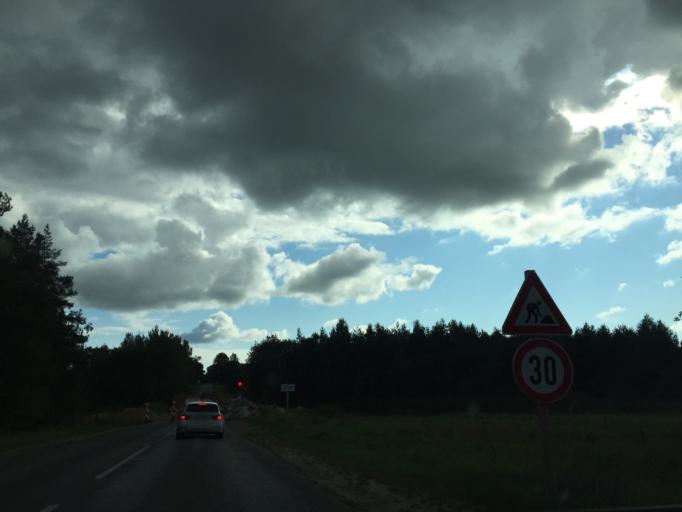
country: LV
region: Limbazu Rajons
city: Limbazi
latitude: 57.3542
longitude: 24.6672
